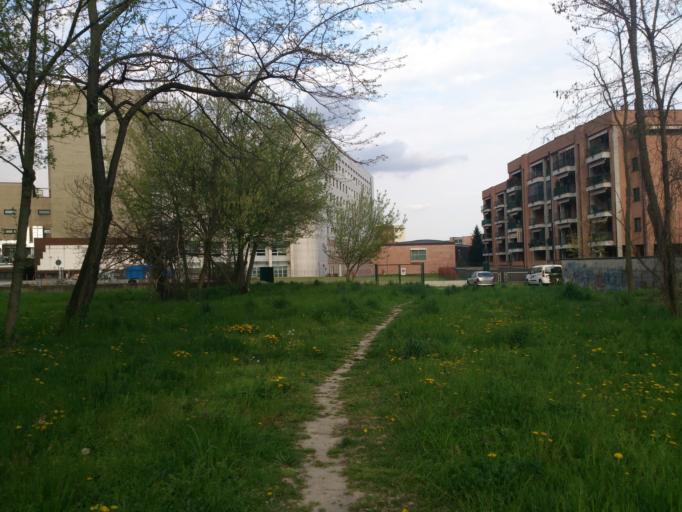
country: IT
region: Lombardy
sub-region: Citta metropolitana di Milano
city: San Donato Milanese
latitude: 45.4111
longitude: 9.2743
